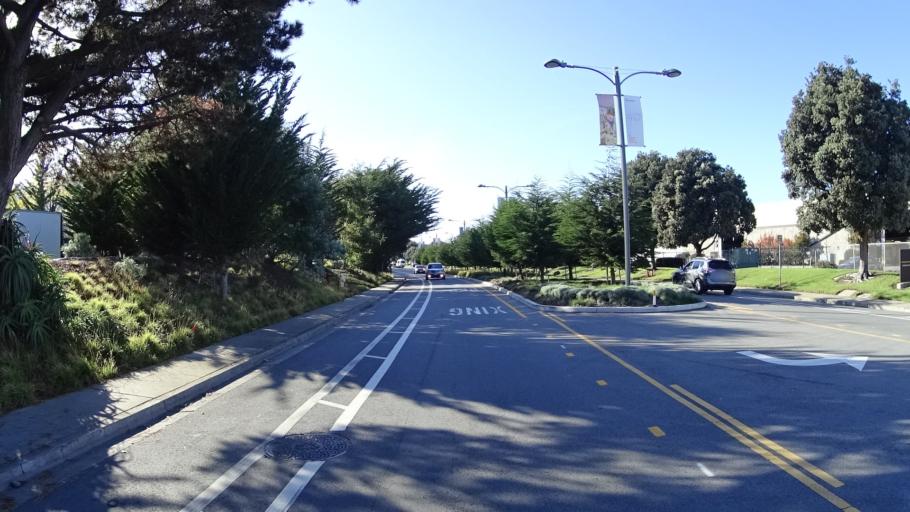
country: US
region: California
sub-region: San Mateo County
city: South San Francisco
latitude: 37.6588
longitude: -122.3810
